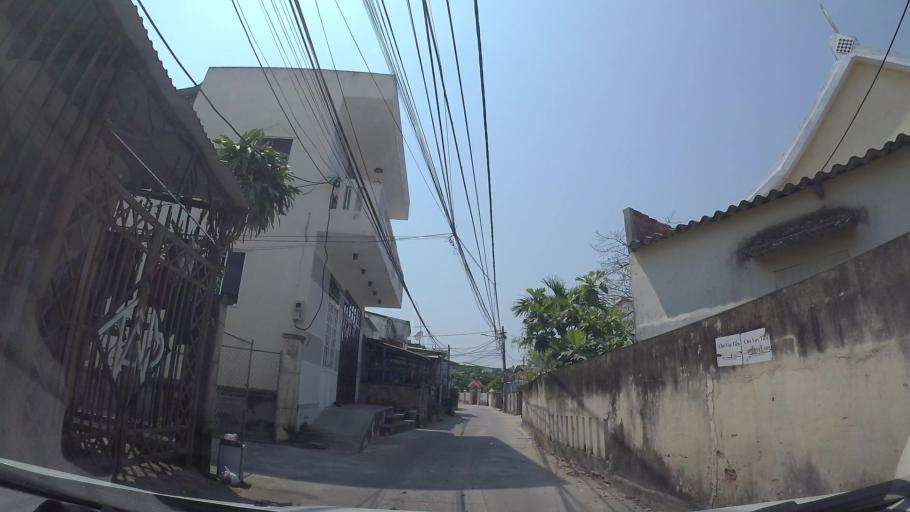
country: VN
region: Da Nang
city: Ngu Hanh Son
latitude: 15.9983
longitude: 108.2629
